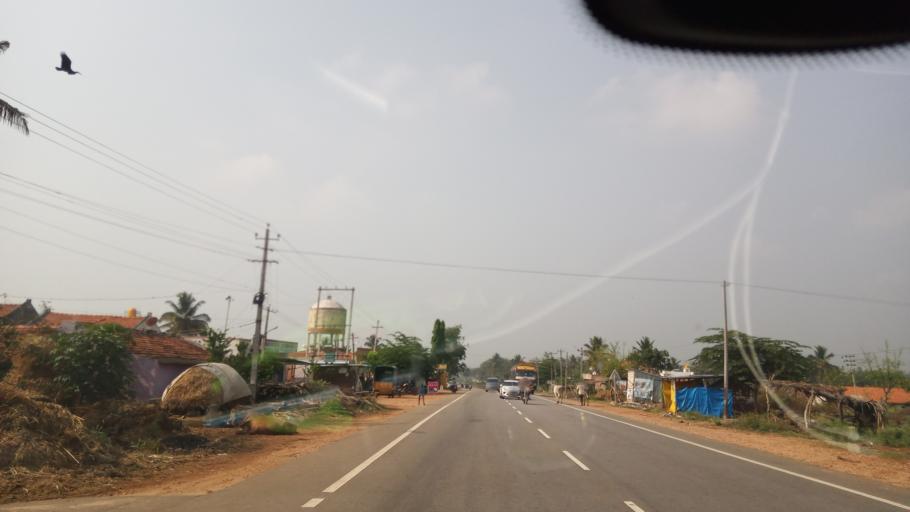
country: IN
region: Karnataka
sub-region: Mandya
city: Pandavapura
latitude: 12.5514
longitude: 76.6719
